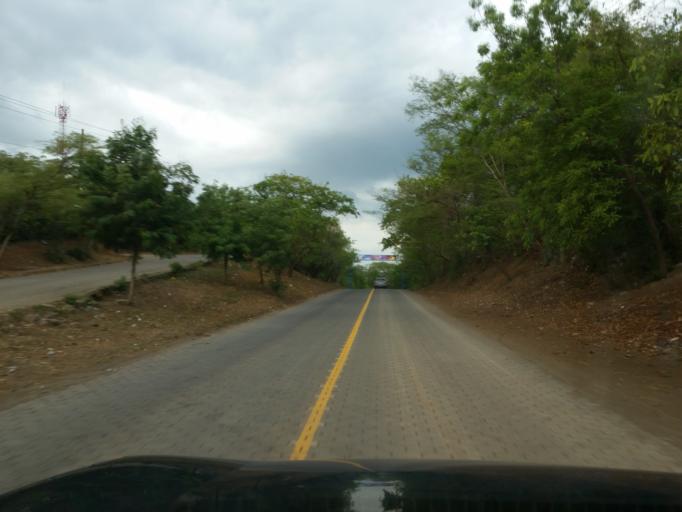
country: NI
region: Managua
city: Carlos Fonseca Amador
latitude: 11.8975
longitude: -86.5127
